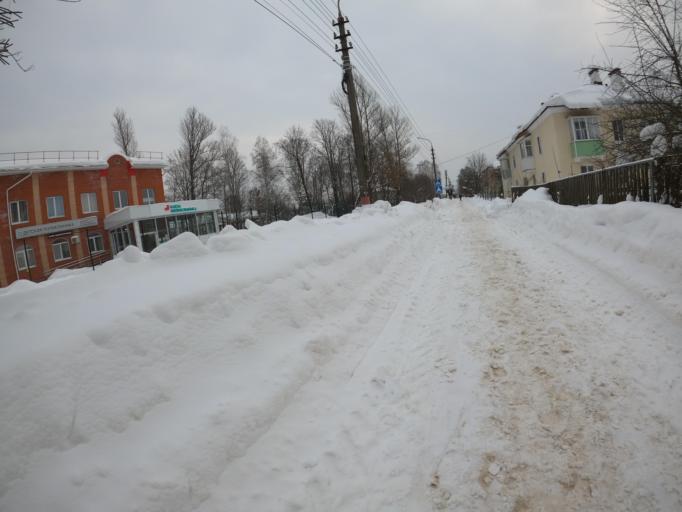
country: RU
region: Moskovskaya
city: Elektrogorsk
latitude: 55.8832
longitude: 38.7893
